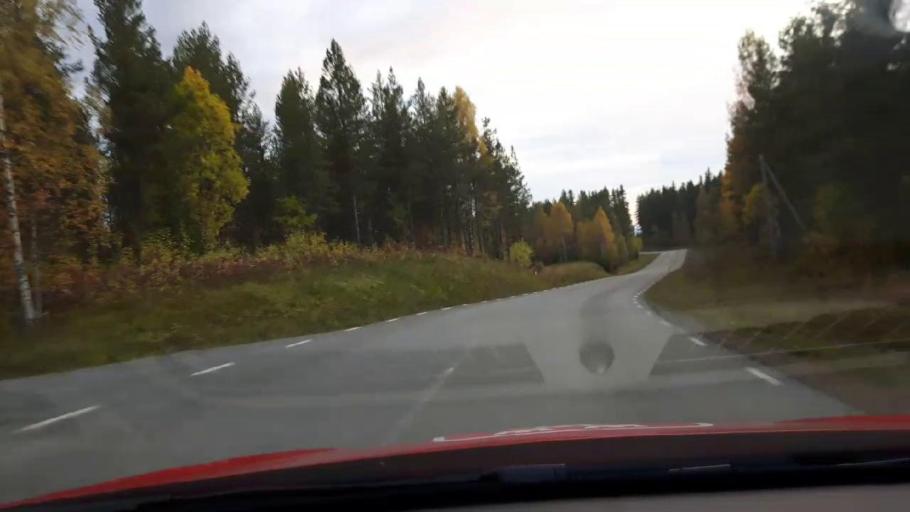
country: SE
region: Jaemtland
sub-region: OEstersunds Kommun
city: Lit
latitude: 63.3158
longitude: 15.1440
